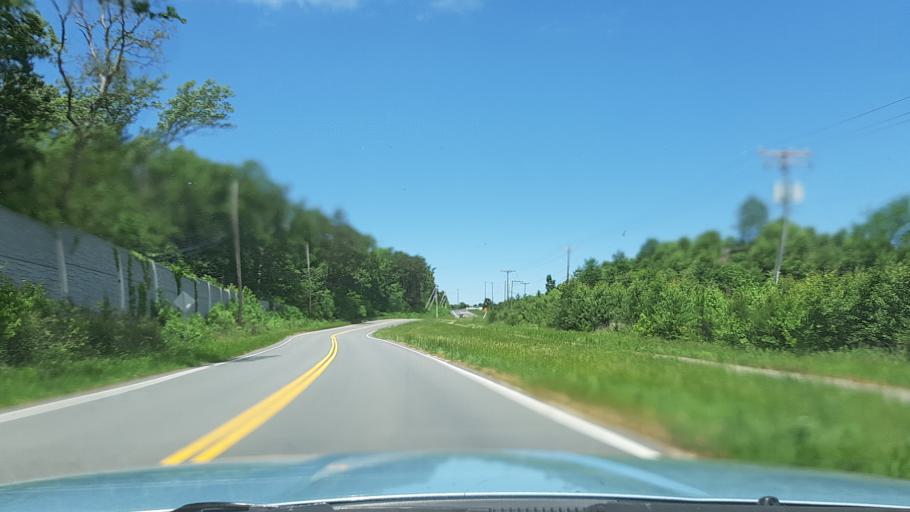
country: US
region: Virginia
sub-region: Fairfax County
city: West Springfield
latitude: 38.7485
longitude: -77.2123
